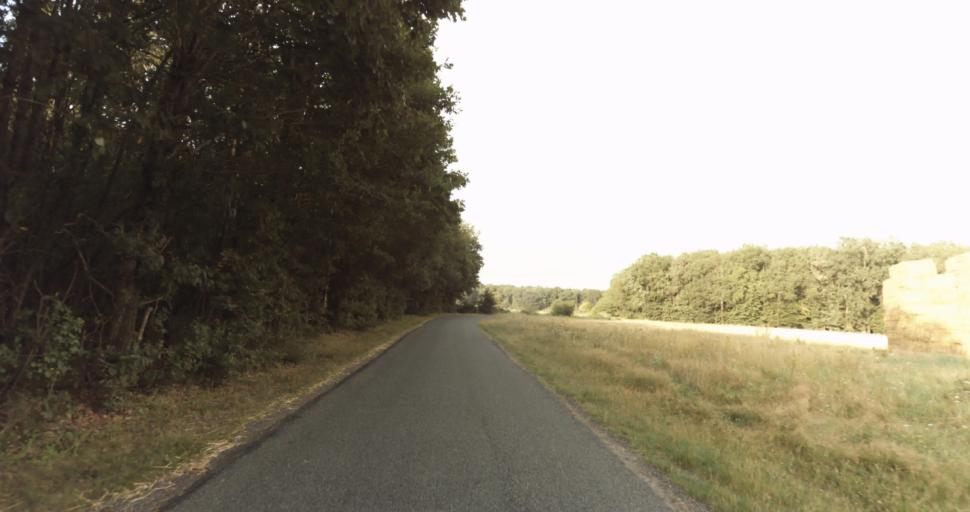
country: FR
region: Centre
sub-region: Departement d'Eure-et-Loir
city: Vert-en-Drouais
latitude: 48.7759
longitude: 1.3193
